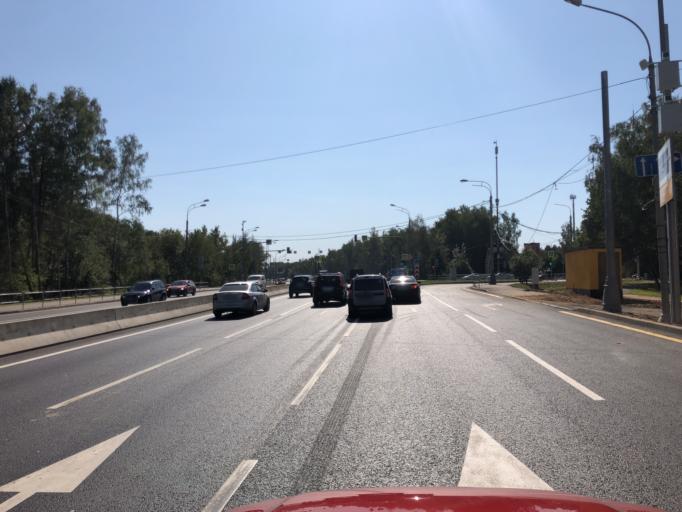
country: RU
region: Moskovskaya
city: Troitsk
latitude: 55.4679
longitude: 37.3031
